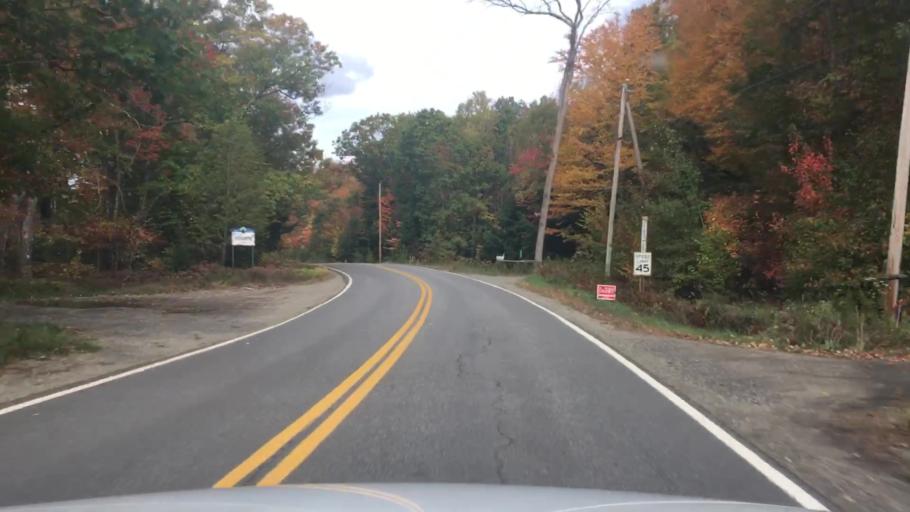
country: US
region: Maine
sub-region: Knox County
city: Hope
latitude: 44.3231
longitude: -69.1284
